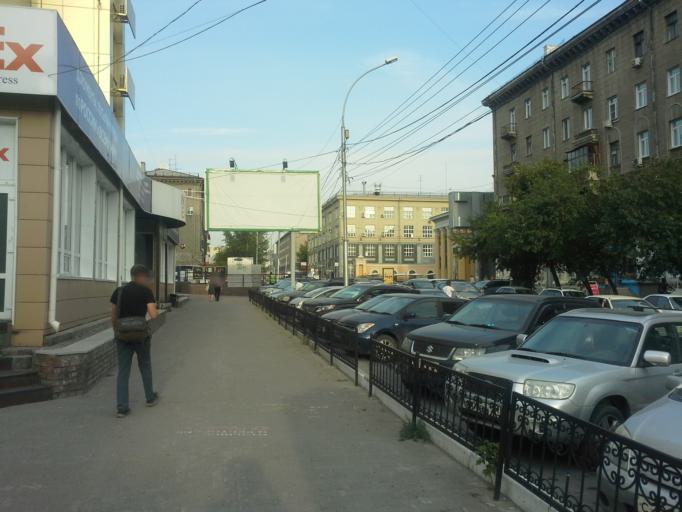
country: RU
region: Novosibirsk
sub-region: Novosibirskiy Rayon
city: Novosibirsk
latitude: 55.0296
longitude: 82.9130
